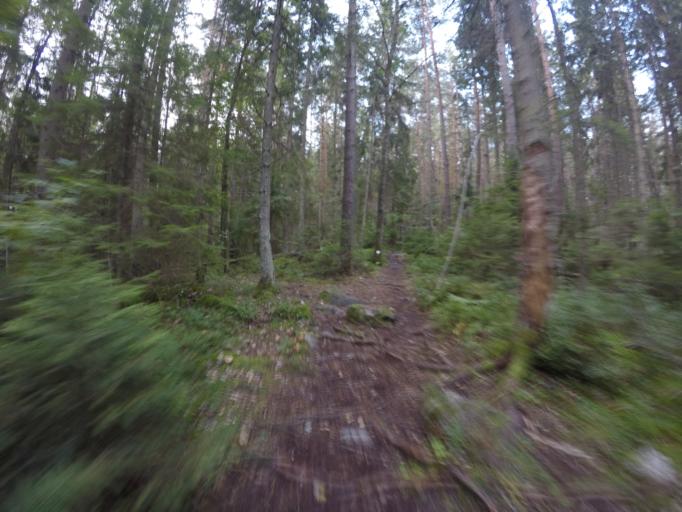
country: SE
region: Vaestmanland
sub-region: Vasteras
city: Vasteras
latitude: 59.6428
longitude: 16.5225
